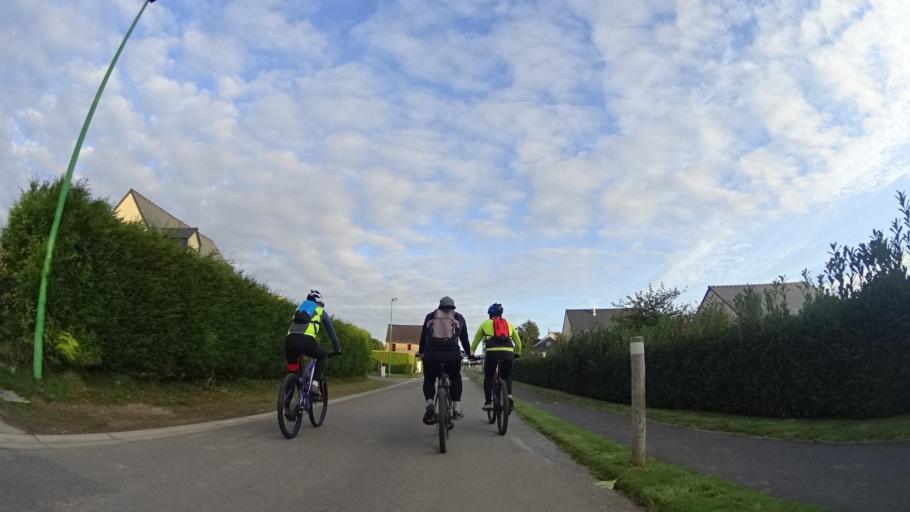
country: FR
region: Brittany
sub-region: Departement des Cotes-d'Armor
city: Evran
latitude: 48.3771
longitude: -1.9686
